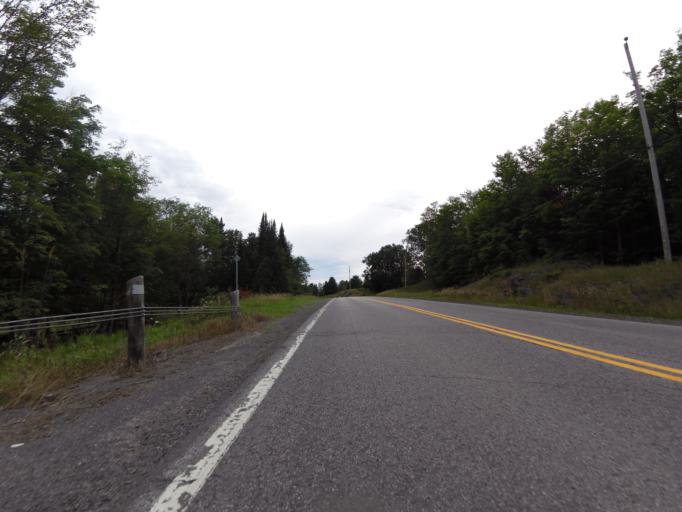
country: CA
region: Ontario
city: Carleton Place
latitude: 45.1093
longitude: -76.3759
